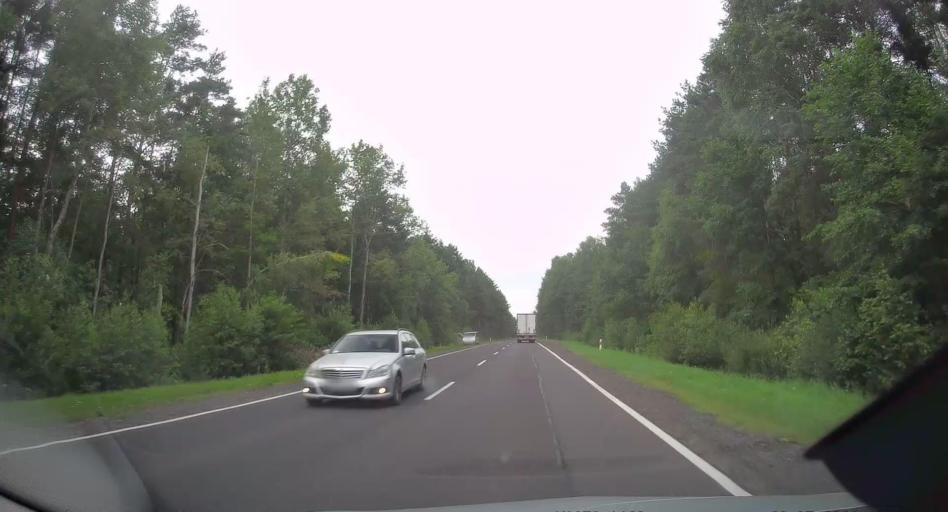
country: PL
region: Lodz Voivodeship
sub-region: Powiat radomszczanski
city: Radomsko
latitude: 51.0280
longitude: 19.4345
